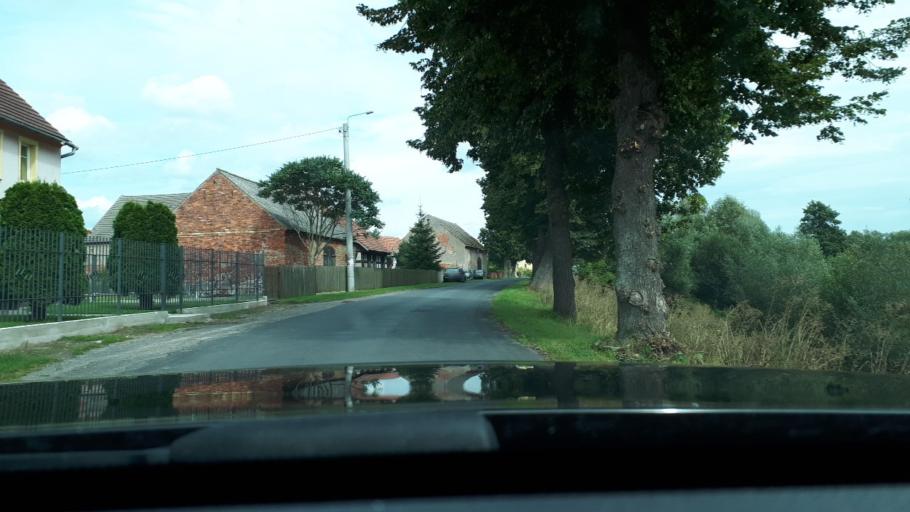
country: PL
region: Lower Silesian Voivodeship
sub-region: Powiat zlotoryjski
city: Zagrodno
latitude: 51.2452
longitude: 15.8520
